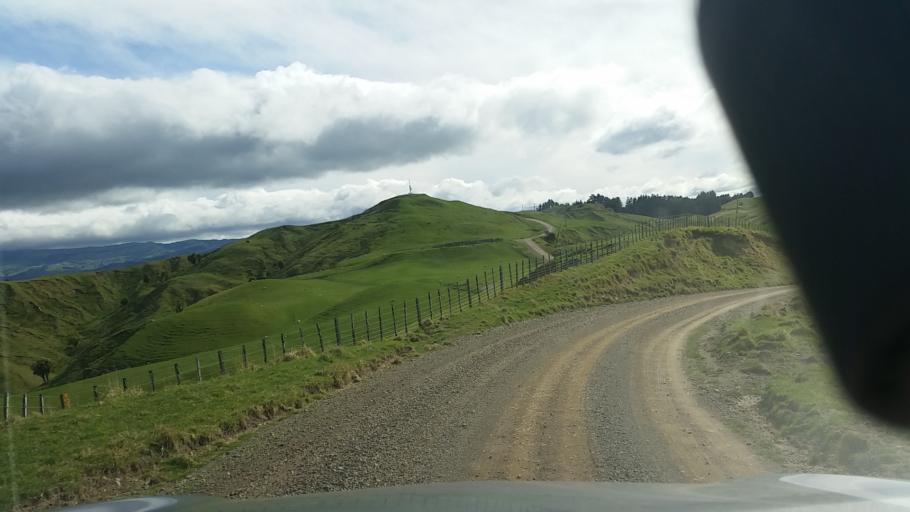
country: NZ
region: Hawke's Bay
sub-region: Napier City
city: Napier
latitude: -39.2084
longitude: 176.9562
